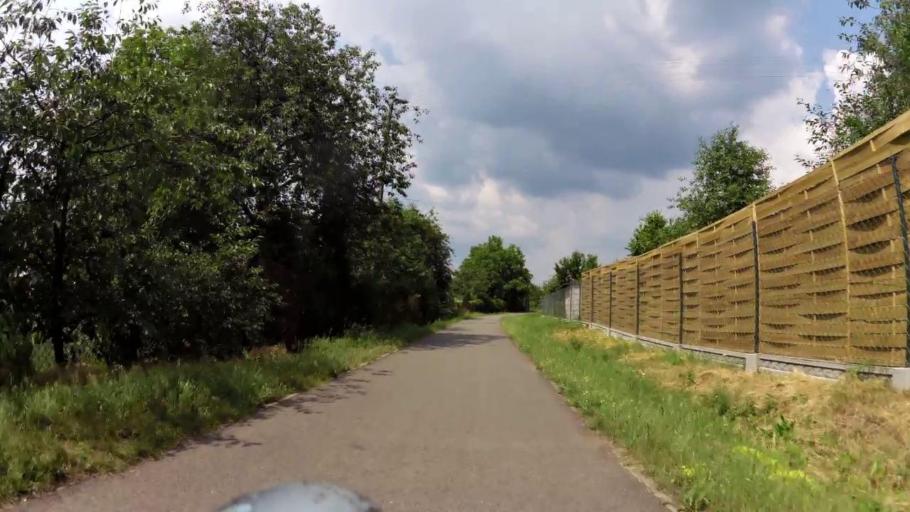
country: PL
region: Kujawsko-Pomorskie
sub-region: Powiat bydgoski
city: Koronowo
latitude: 53.3034
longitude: 17.9448
